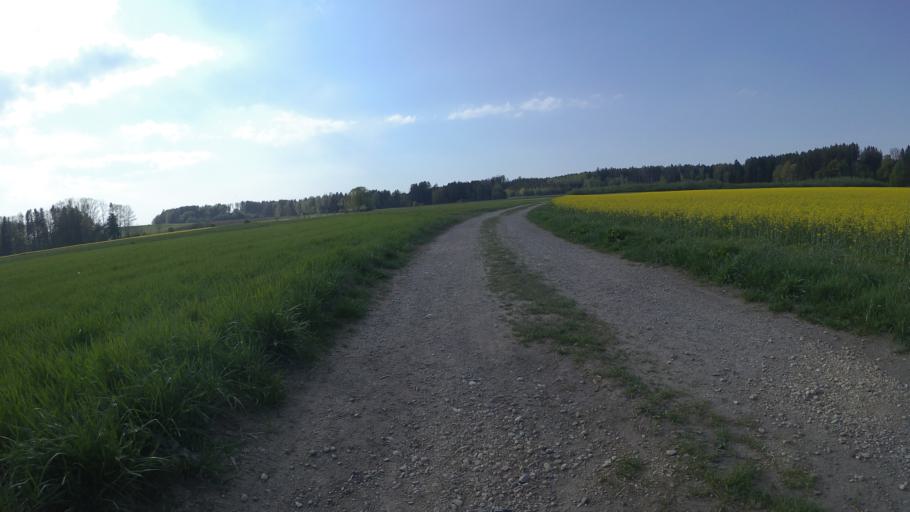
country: DE
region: Bavaria
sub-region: Upper Bavaria
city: Chieming
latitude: 47.9106
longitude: 12.5143
